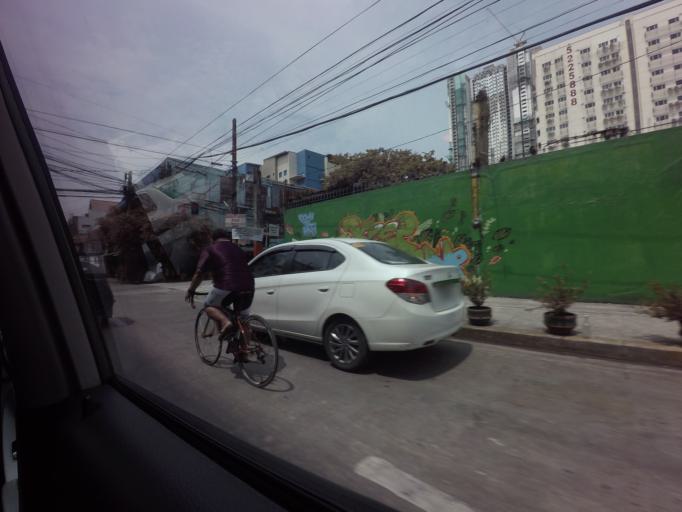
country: PH
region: Metro Manila
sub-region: City of Manila
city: Quiapo
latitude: 14.5760
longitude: 120.9910
